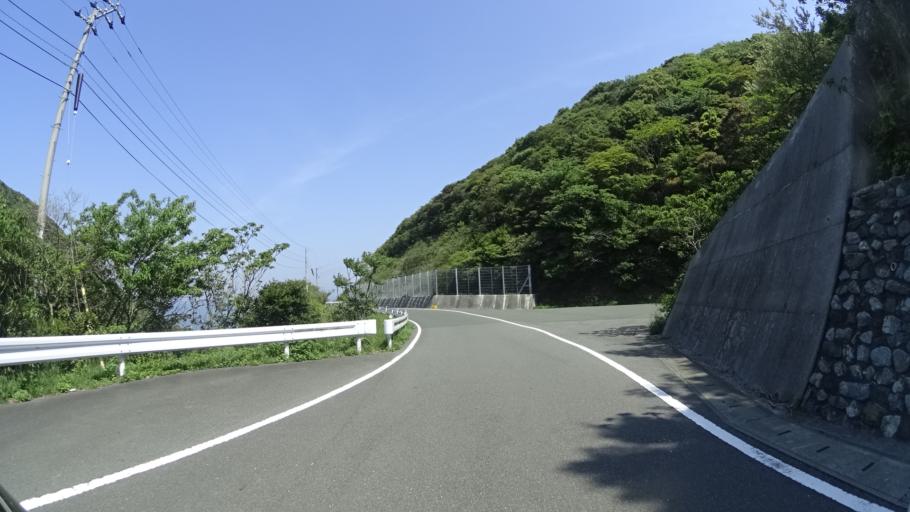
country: JP
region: Oita
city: Tsukumiura
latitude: 33.3560
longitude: 132.0385
